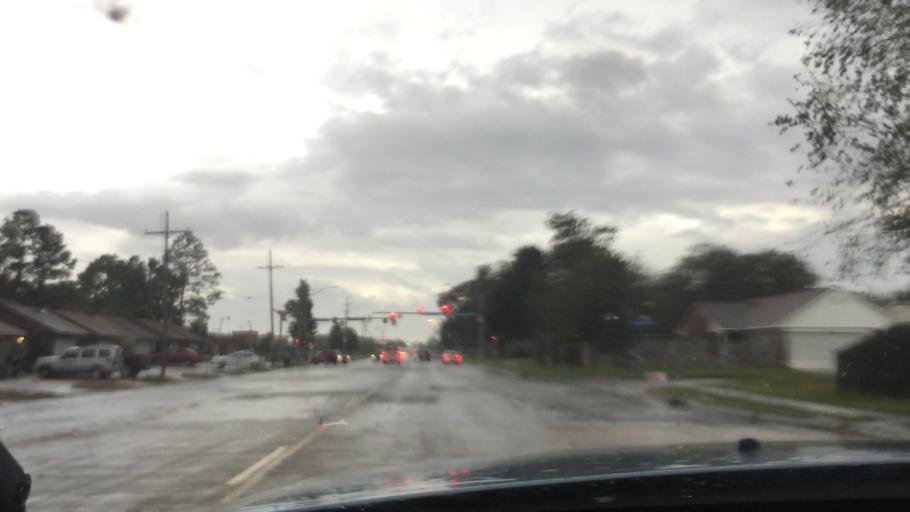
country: US
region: Louisiana
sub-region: East Baton Rouge Parish
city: Monticello
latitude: 30.4479
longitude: -91.0245
